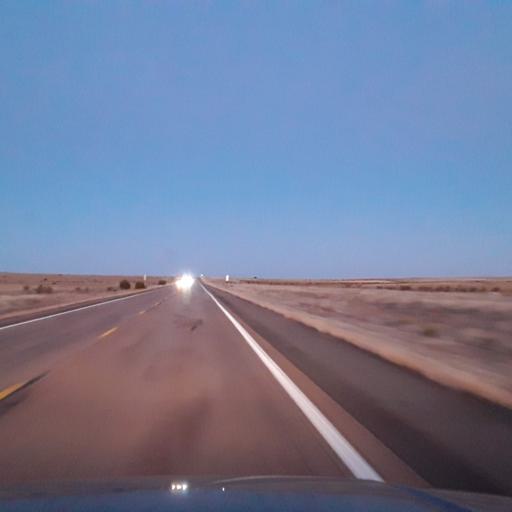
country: US
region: New Mexico
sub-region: Guadalupe County
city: Santa Rosa
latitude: 34.7647
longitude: -104.9796
